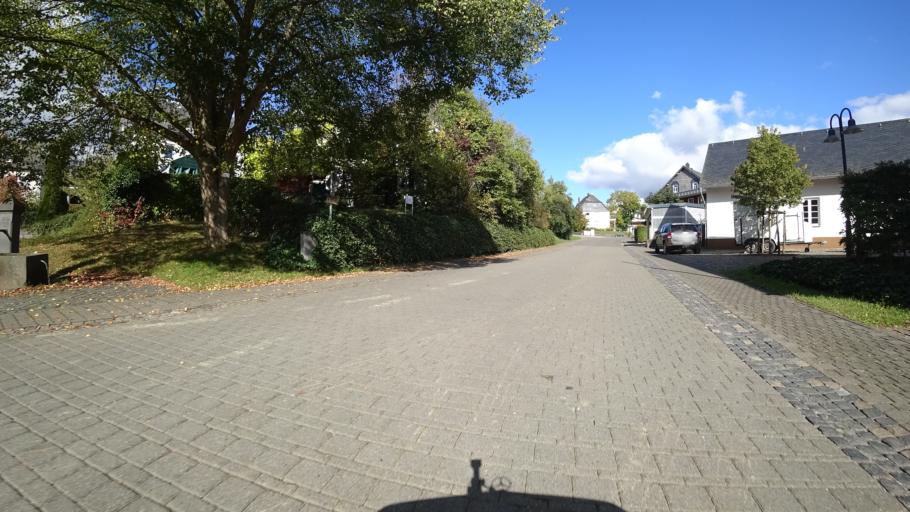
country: DE
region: Rheinland-Pfalz
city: Neuerkirch
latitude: 50.0146
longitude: 7.4912
